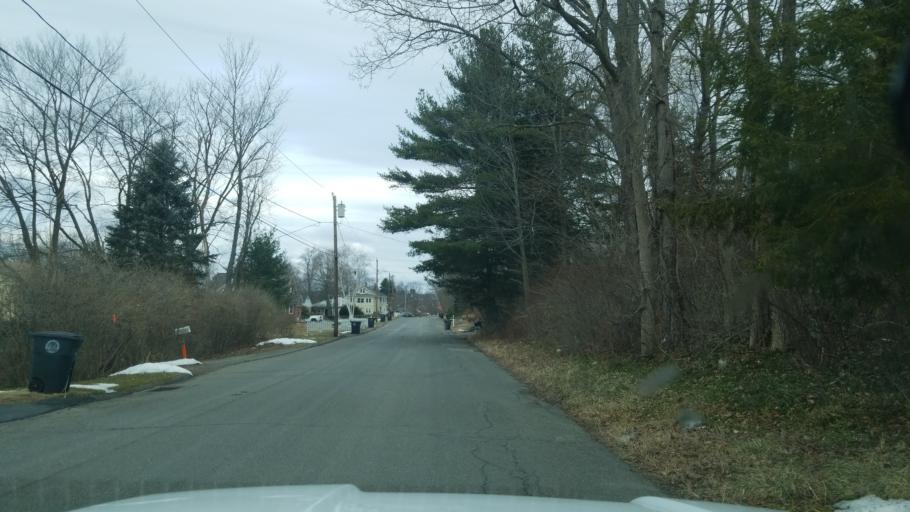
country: US
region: Connecticut
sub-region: Litchfield County
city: Torrington
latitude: 41.7969
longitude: -73.1047
